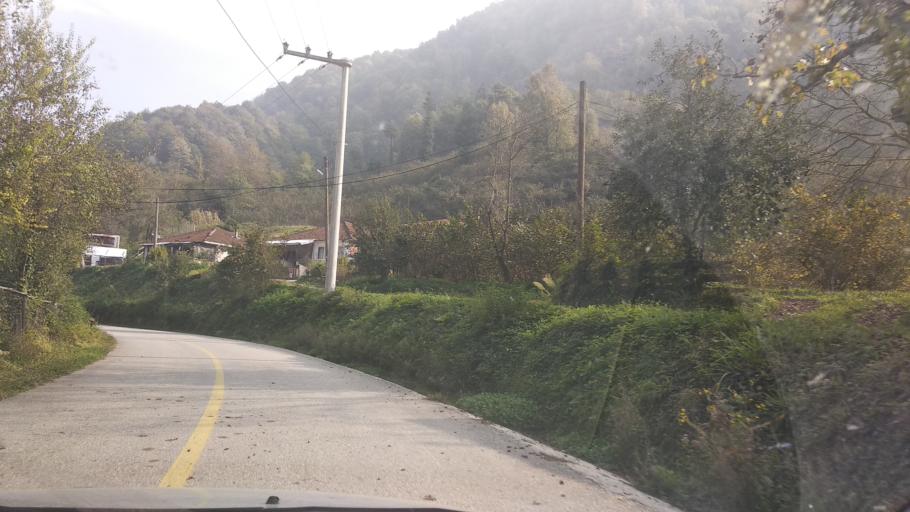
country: TR
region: Duzce
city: Kaynasli
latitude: 40.7343
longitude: 31.2144
